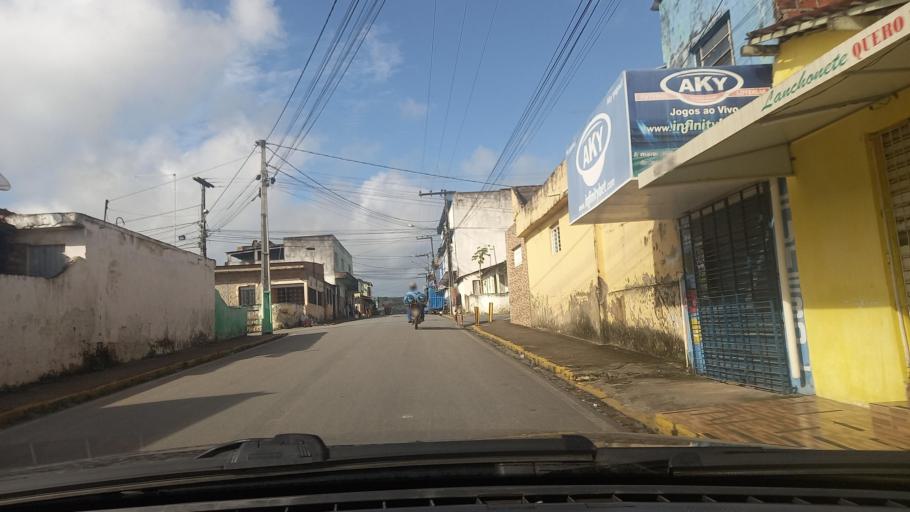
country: BR
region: Pernambuco
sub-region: Vitoria De Santo Antao
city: Vitoria de Santo Antao
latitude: -8.1171
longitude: -35.2787
